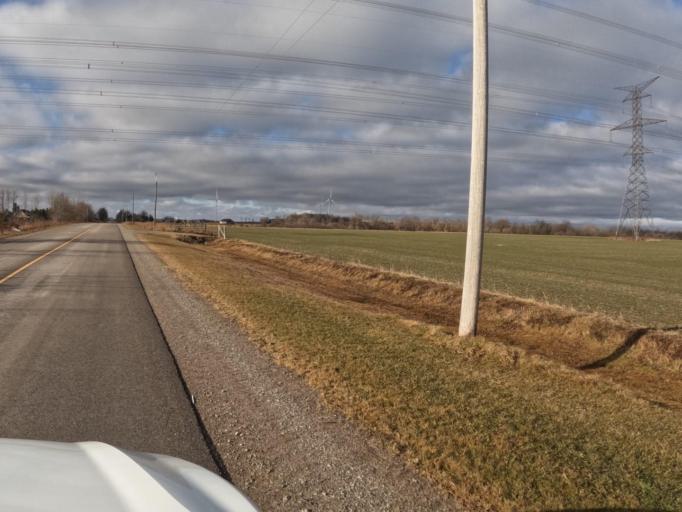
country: CA
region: Ontario
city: Shelburne
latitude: 43.8932
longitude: -80.3435
